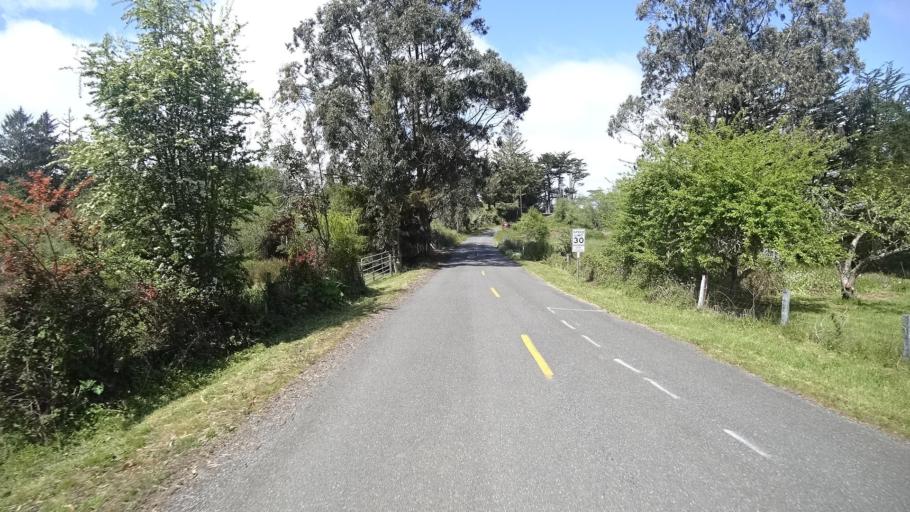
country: US
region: California
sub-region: Humboldt County
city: Humboldt Hill
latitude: 40.6736
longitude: -124.2190
